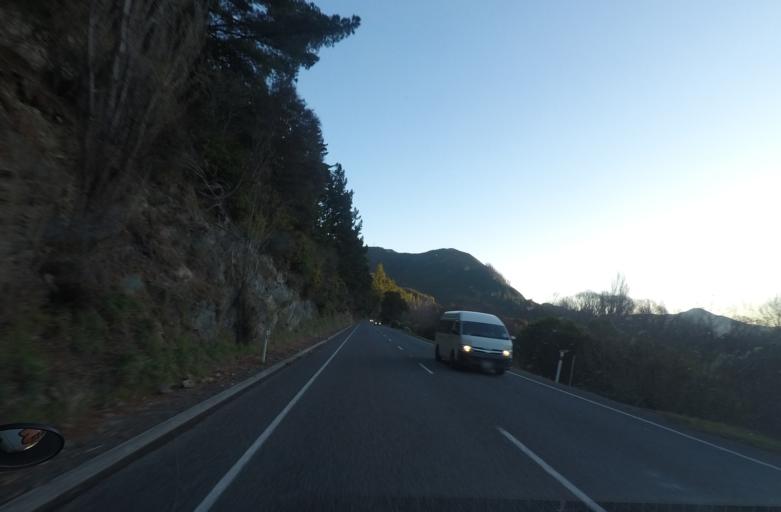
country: NZ
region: Marlborough
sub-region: Marlborough District
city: Picton
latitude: -41.2857
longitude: 173.7097
